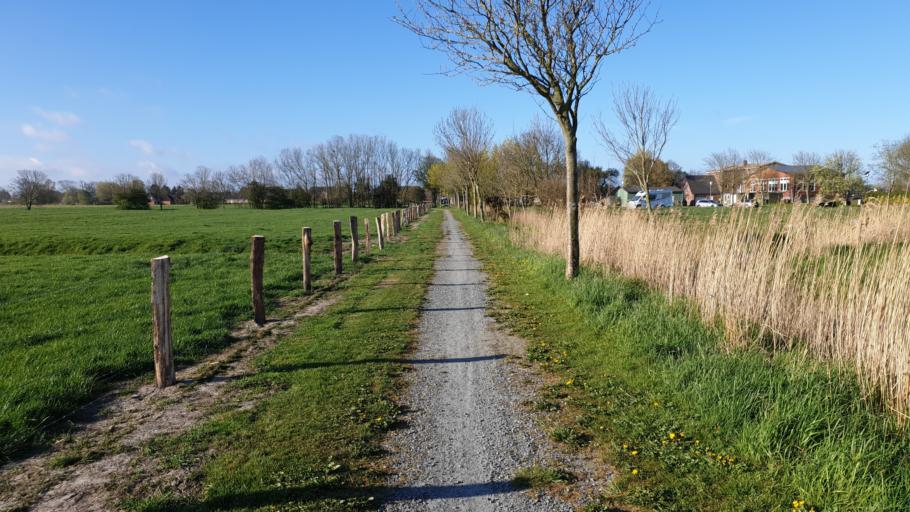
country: DE
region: Schleswig-Holstein
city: Elisabeth-Sophien-Koog
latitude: 54.4889
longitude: 8.8617
